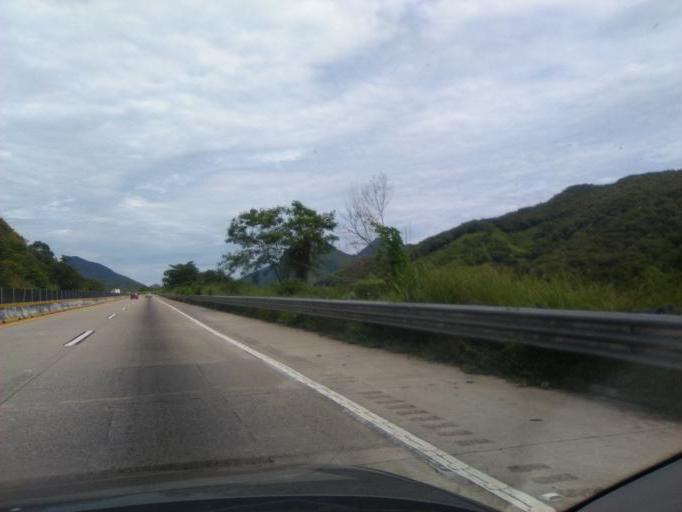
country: MX
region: Guerrero
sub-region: Chilpancingo de los Bravo
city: Julian Blanco (Dos Caminos)
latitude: 17.2126
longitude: -99.5345
